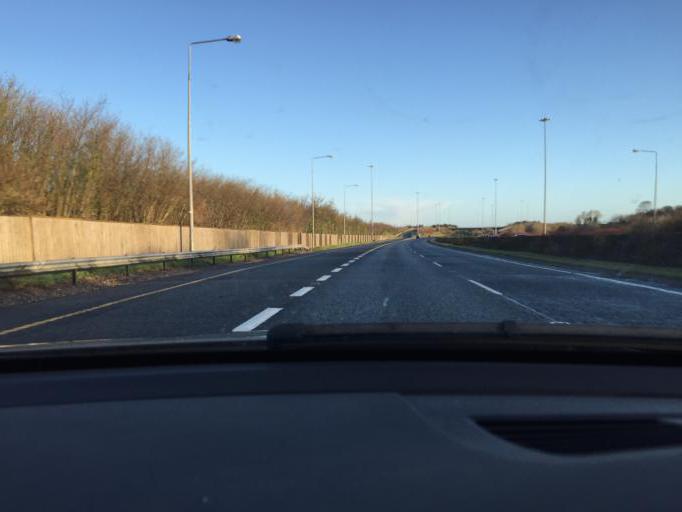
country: IE
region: Leinster
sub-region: Lu
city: Dunleer
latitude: 53.8524
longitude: -6.4261
